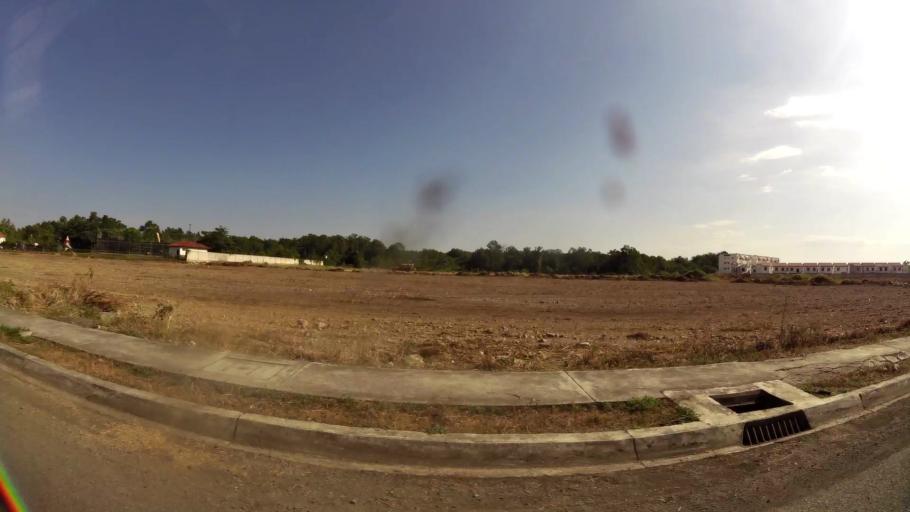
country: EC
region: Guayas
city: Santa Lucia
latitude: -2.1903
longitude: -80.0002
